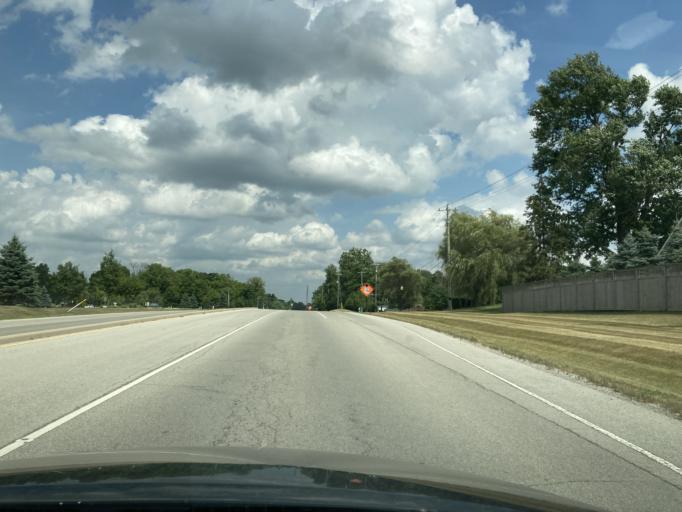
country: US
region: Indiana
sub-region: Boone County
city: Zionsville
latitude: 39.9986
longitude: -86.2487
